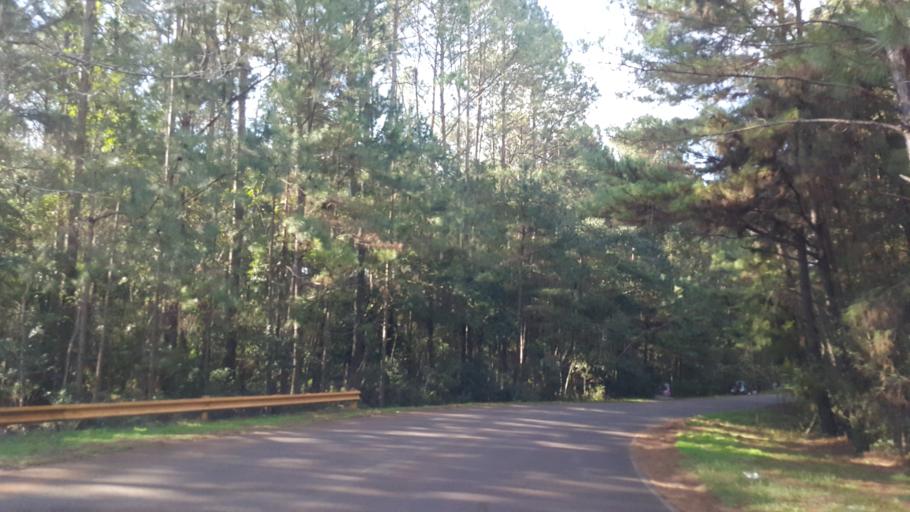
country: AR
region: Misiones
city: Puerto Leoni
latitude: -27.0057
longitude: -55.1899
